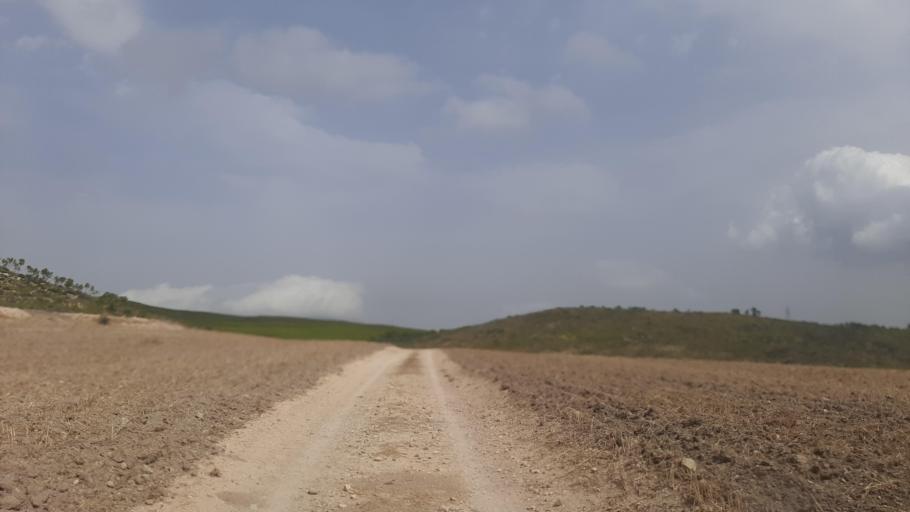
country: TN
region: Zaghwan
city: El Fahs
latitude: 36.1958
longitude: 9.8449
